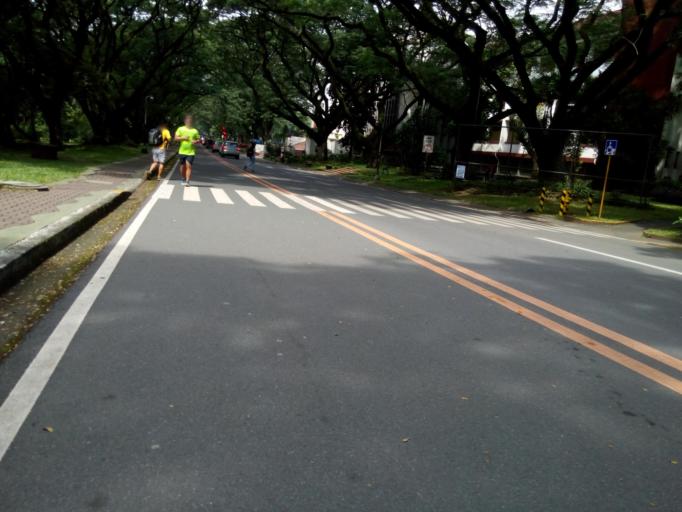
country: PH
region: Metro Manila
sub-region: Quezon City
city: Quezon City
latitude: 14.6562
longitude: 121.0707
